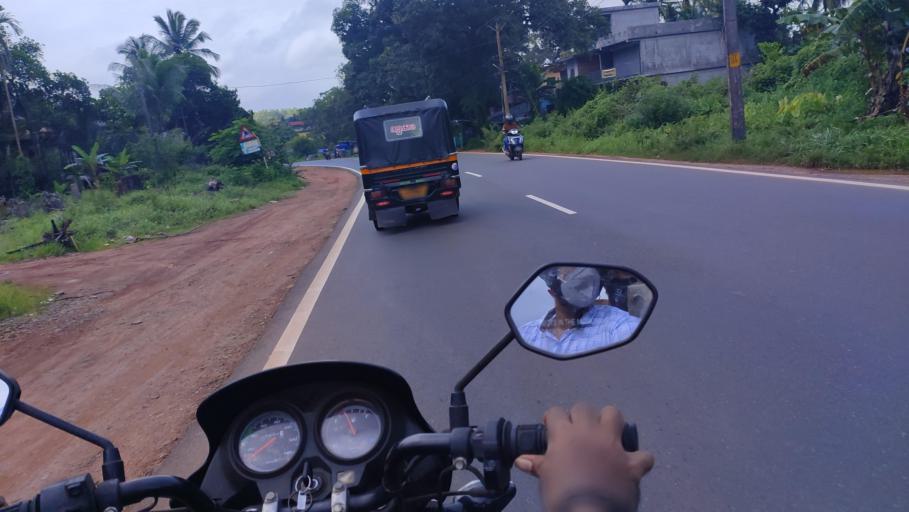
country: IN
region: Kerala
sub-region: Kasaragod District
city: Nileshwar
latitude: 12.2241
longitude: 75.1585
